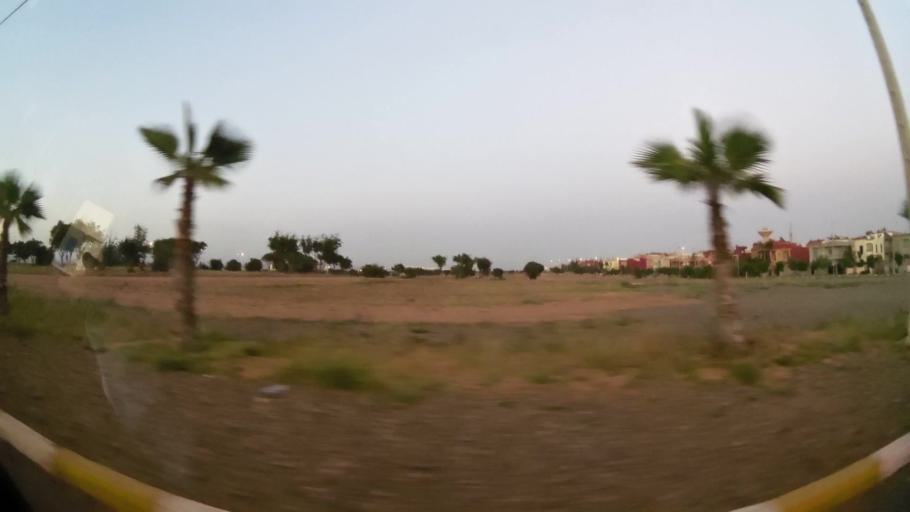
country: MA
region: Souss-Massa-Draa
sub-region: Inezgane-Ait Mellou
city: Inezgane
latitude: 30.3856
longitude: -9.4853
